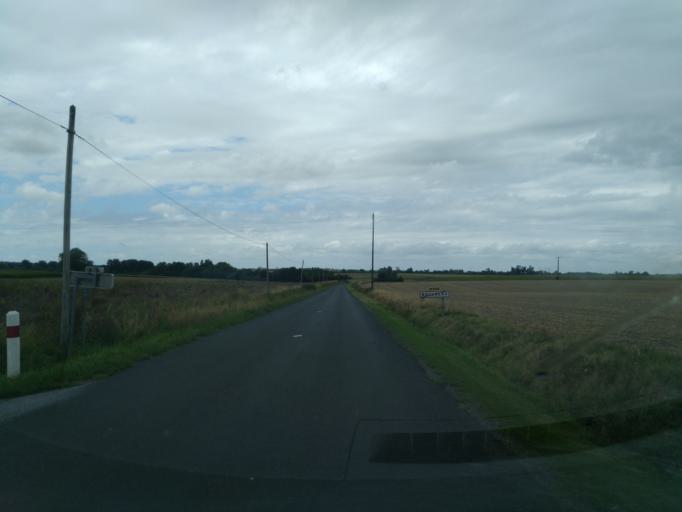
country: FR
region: Poitou-Charentes
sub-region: Departement de la Charente-Maritime
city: Pons
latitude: 45.6010
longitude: -0.5153
